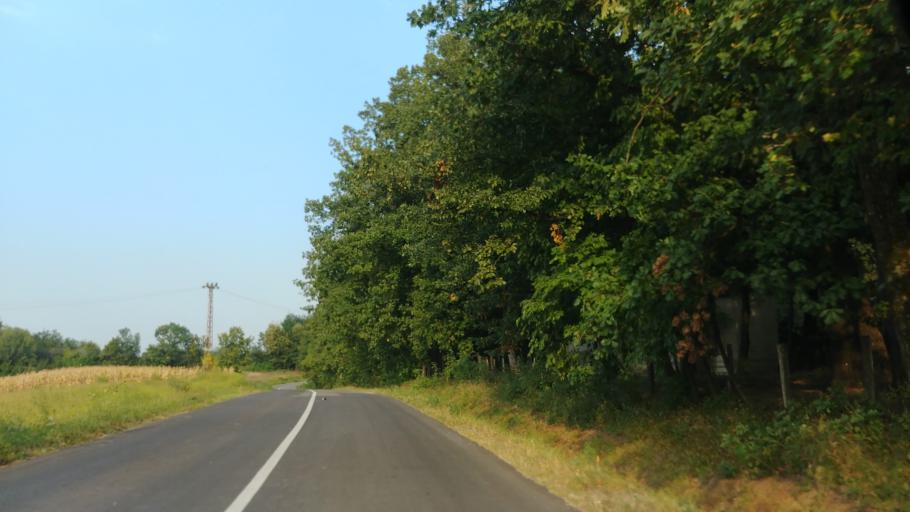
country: BA
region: Republika Srpska
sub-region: Opstina Ugljevik
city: Ugljevik
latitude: 44.7068
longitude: 18.9742
